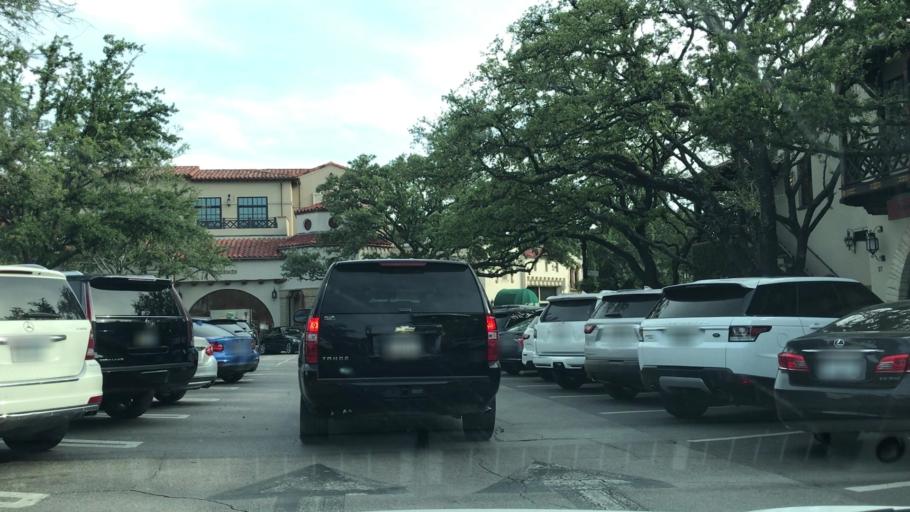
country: US
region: Texas
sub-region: Dallas County
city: Highland Park
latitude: 32.8359
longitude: -96.8064
